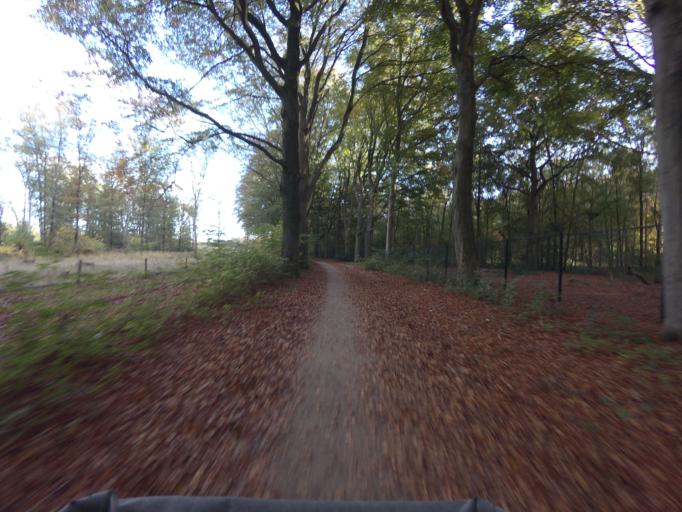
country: NL
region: North Holland
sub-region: Gemeente Hilversum
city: Hilversum
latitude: 52.1884
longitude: 5.1800
